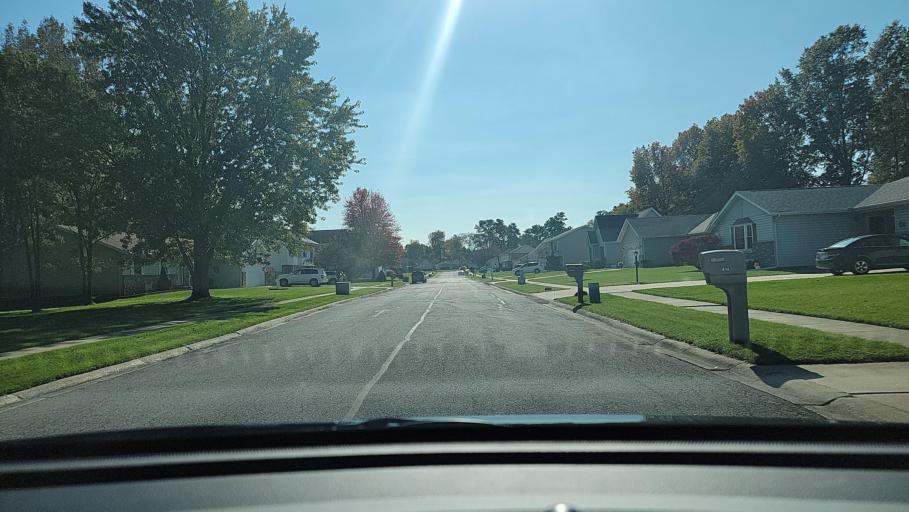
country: US
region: Indiana
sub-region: Porter County
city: Portage
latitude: 41.5821
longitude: -87.1608
